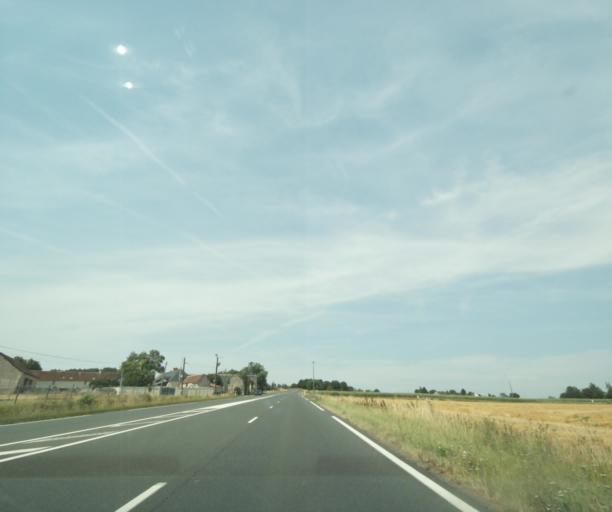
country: FR
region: Centre
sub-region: Departement d'Indre-et-Loire
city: La Celle-Saint-Avant
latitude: 47.0540
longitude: 0.6149
